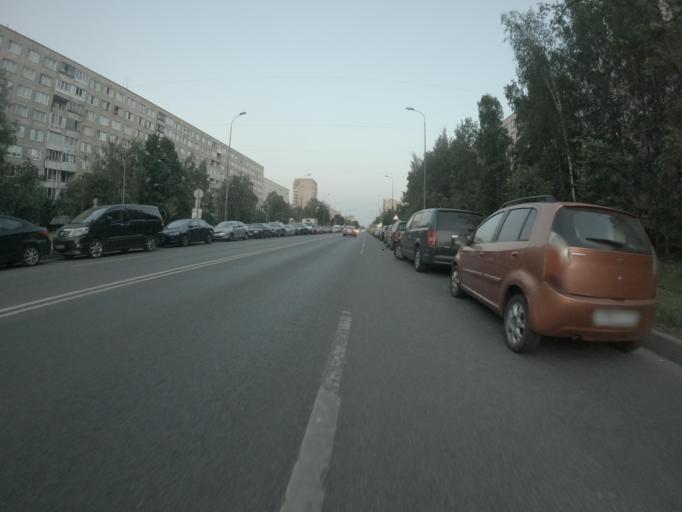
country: RU
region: St.-Petersburg
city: Krasnogvargeisky
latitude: 59.9198
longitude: 30.4806
